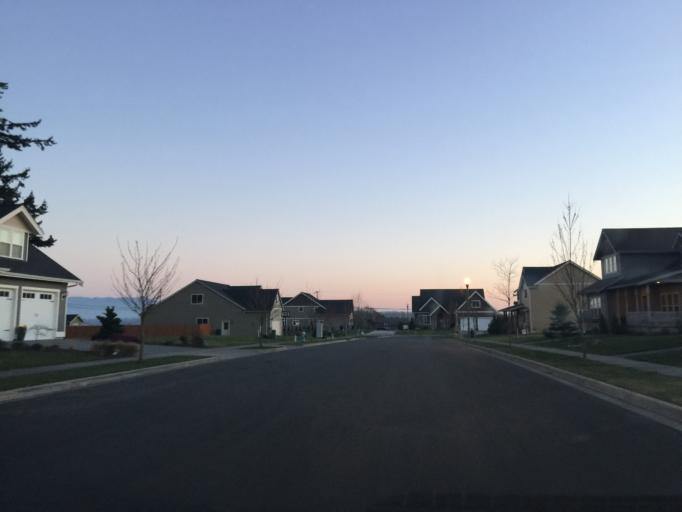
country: US
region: Washington
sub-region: Whatcom County
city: Lynden
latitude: 48.9546
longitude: -122.4198
